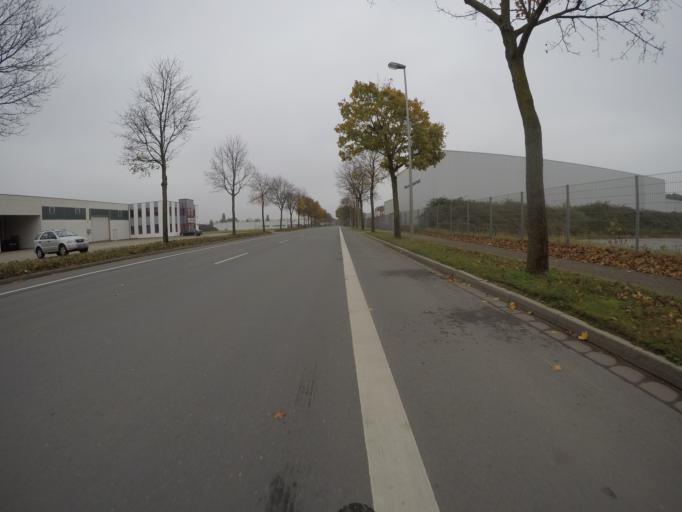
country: DE
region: North Rhine-Westphalia
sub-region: Regierungsbezirk Dusseldorf
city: Bocholt
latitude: 51.8120
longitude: 6.5530
